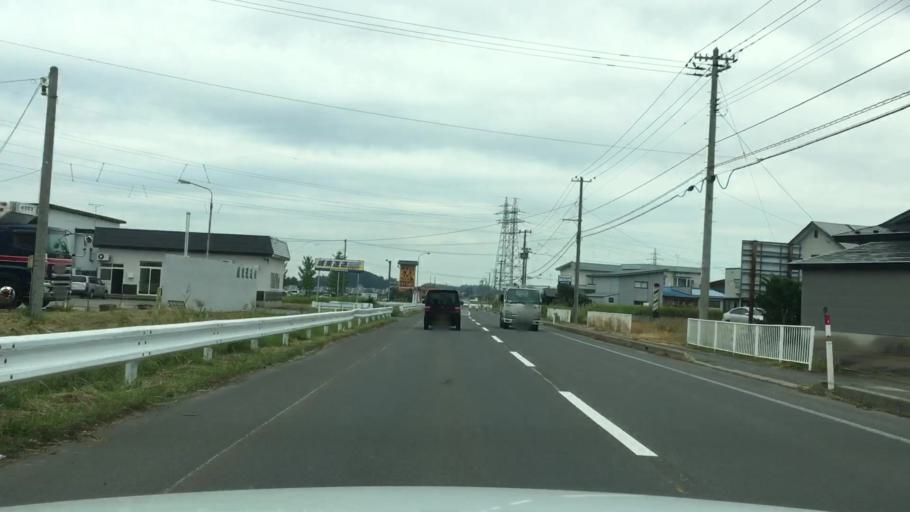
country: JP
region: Aomori
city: Hirosaki
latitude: 40.6320
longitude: 140.4516
